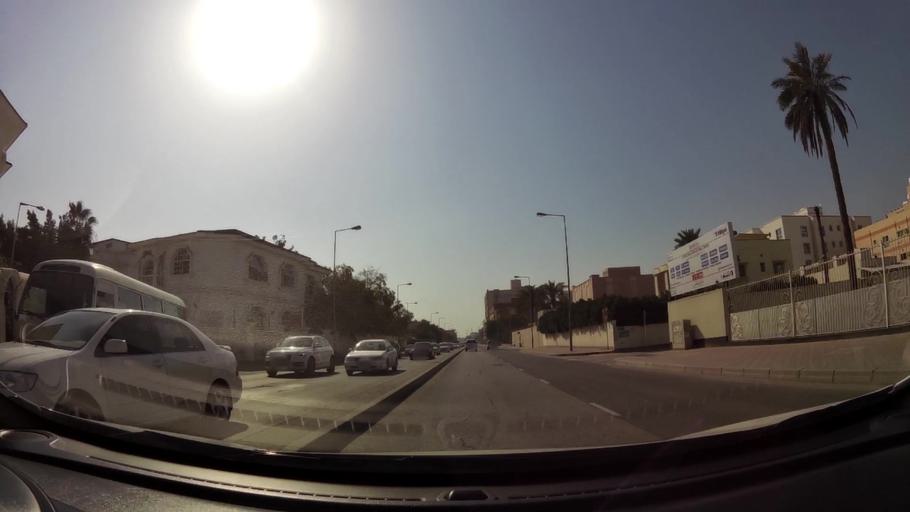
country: BH
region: Manama
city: Manama
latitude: 26.2175
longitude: 50.5798
